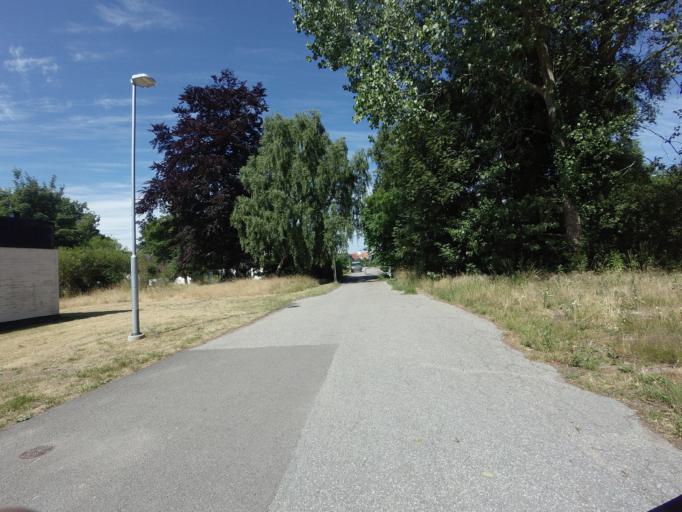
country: SE
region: Skane
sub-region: Vellinge Kommun
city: Skanor med Falsterbo
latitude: 55.4171
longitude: 12.8515
